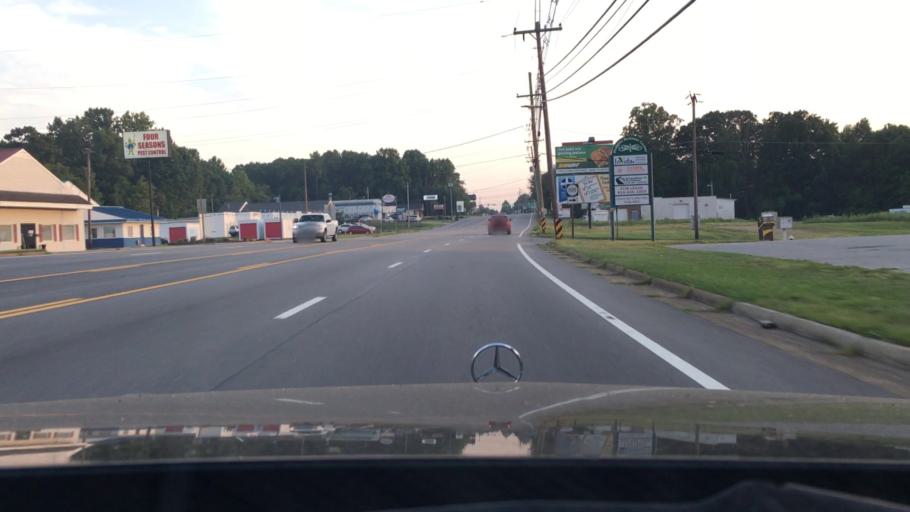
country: US
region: Virginia
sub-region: Pittsylvania County
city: Mount Hermon
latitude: 36.6410
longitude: -79.3832
